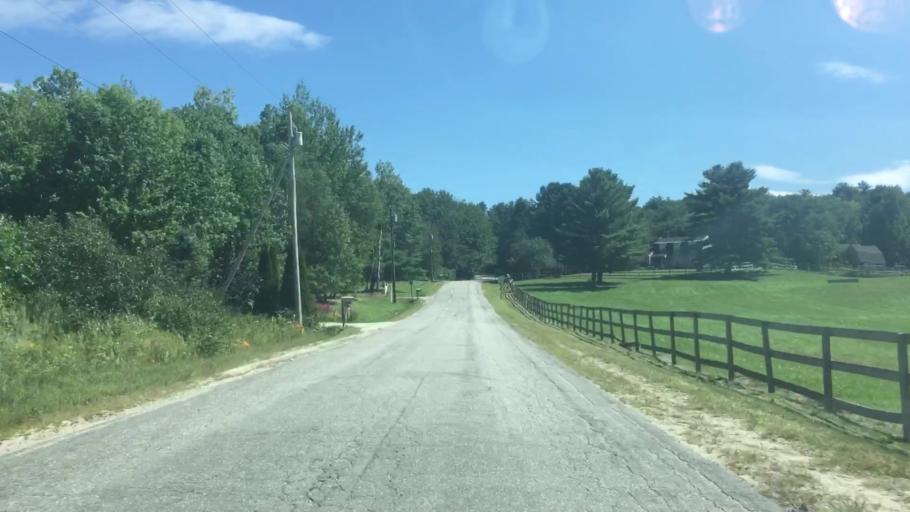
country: US
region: Maine
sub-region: Androscoggin County
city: Sabattus
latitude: 44.1227
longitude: -70.0623
